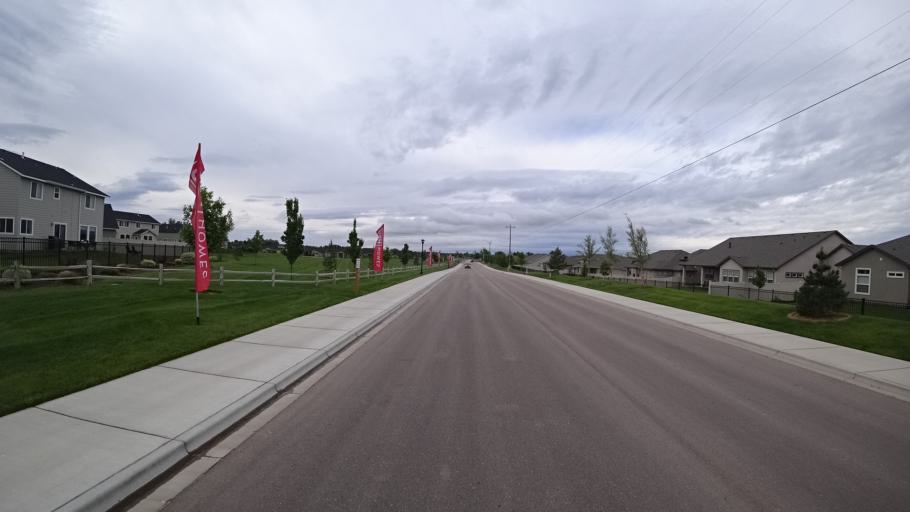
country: US
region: Idaho
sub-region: Ada County
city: Star
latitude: 43.7124
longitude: -116.5032
